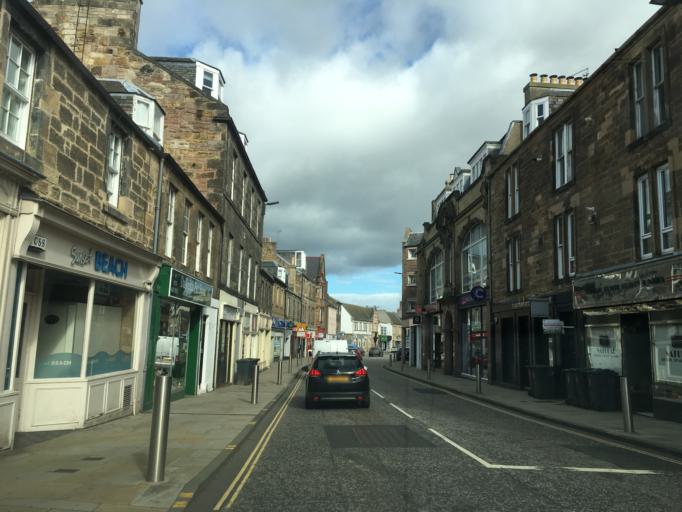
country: GB
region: Scotland
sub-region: Midlothian
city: Dalkeith
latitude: 55.8932
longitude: -3.0724
